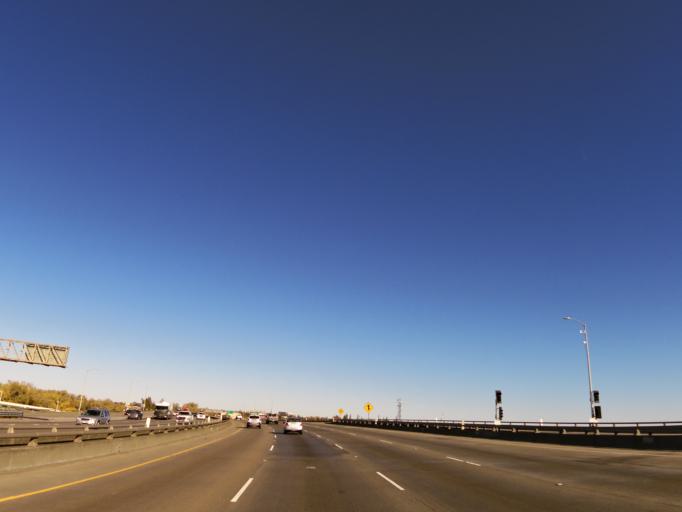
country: US
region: California
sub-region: Sacramento County
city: Sacramento
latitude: 38.5855
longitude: -121.5028
